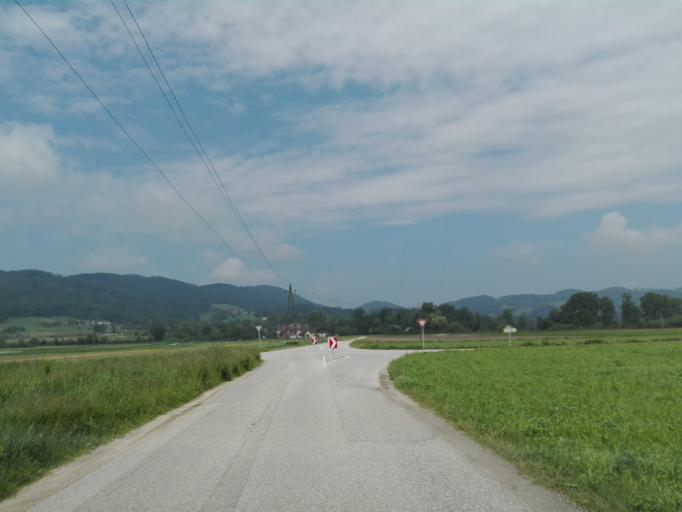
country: AT
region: Upper Austria
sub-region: Politischer Bezirk Urfahr-Umgebung
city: Feldkirchen an der Donau
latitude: 48.3542
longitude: 13.9886
